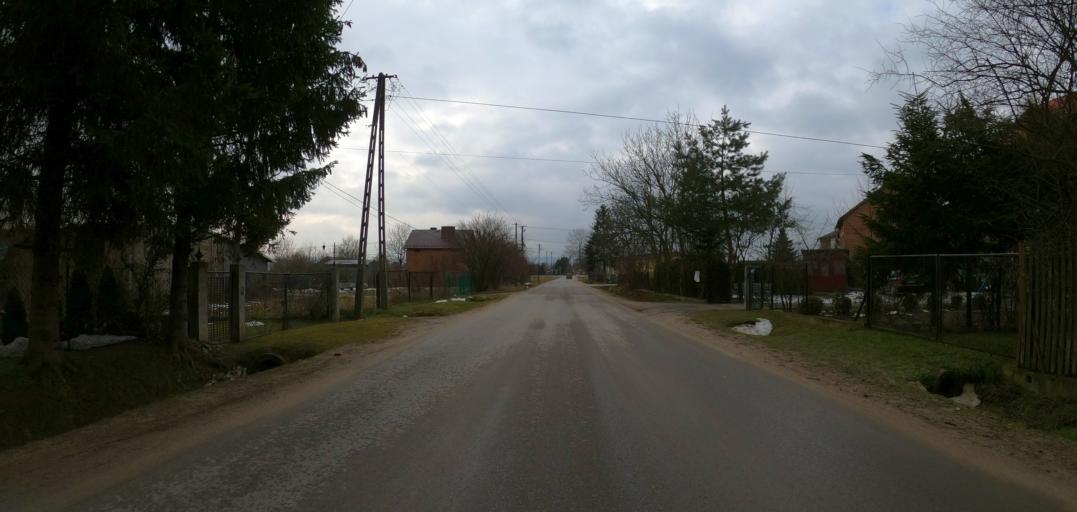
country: PL
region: Subcarpathian Voivodeship
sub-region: Powiat debicki
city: Pilzno
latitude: 49.9816
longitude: 21.3356
